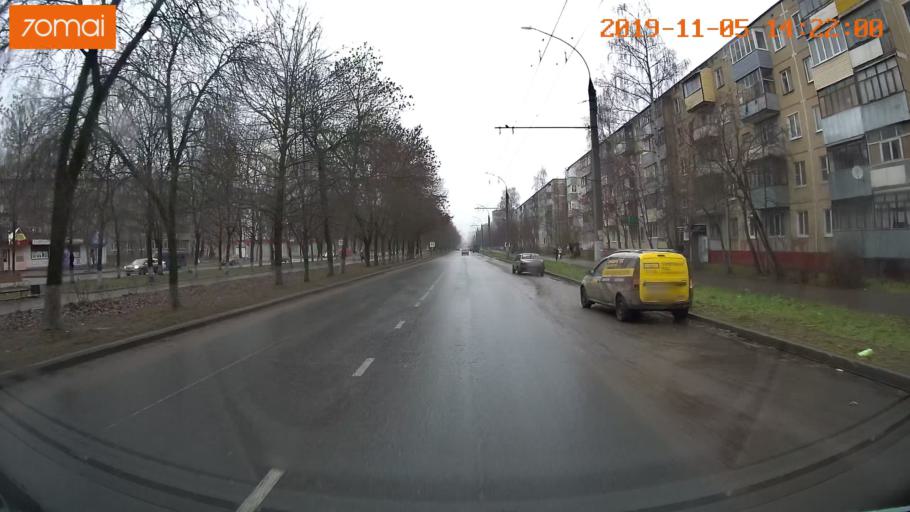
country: RU
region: Ivanovo
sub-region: Gorod Ivanovo
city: Ivanovo
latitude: 56.9613
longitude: 41.0076
